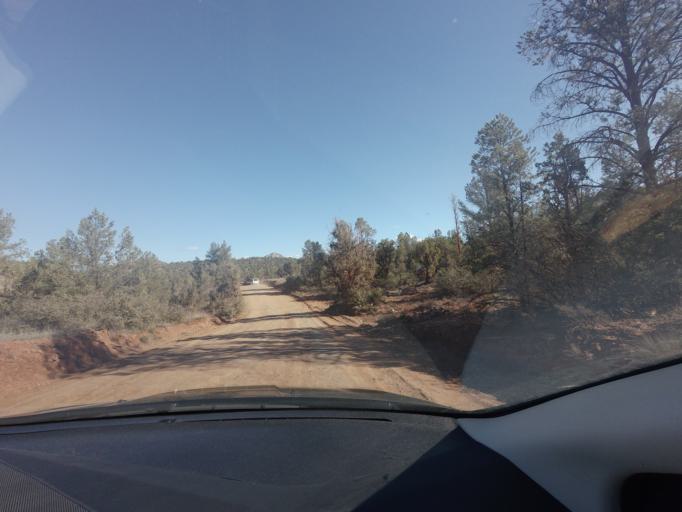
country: US
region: Arizona
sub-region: Yavapai County
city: West Sedona
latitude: 34.8155
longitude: -111.8112
